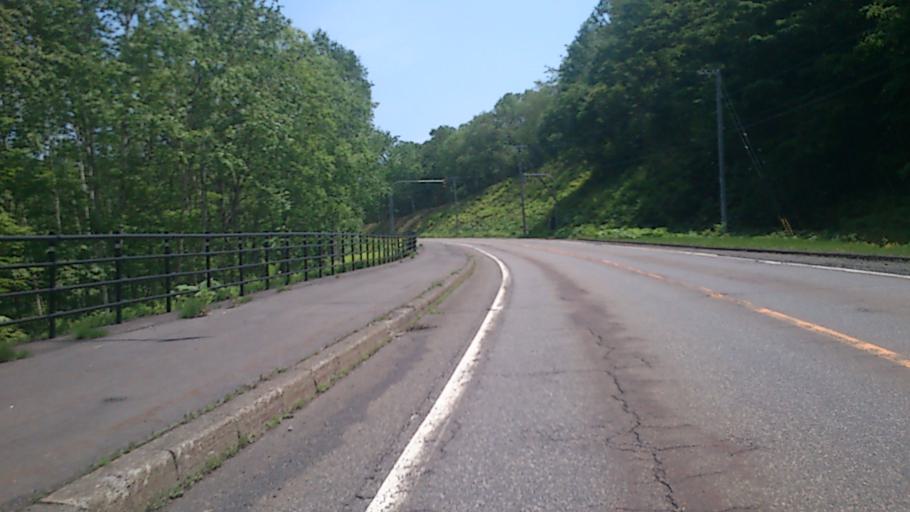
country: JP
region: Hokkaido
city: Otofuke
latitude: 43.3614
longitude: 143.2471
